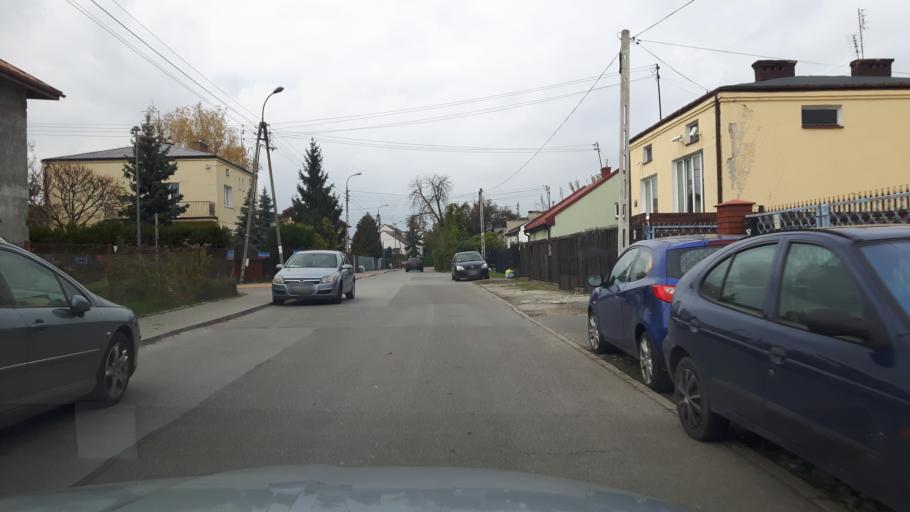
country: PL
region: Masovian Voivodeship
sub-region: Warszawa
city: Targowek
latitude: 52.2863
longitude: 21.0729
